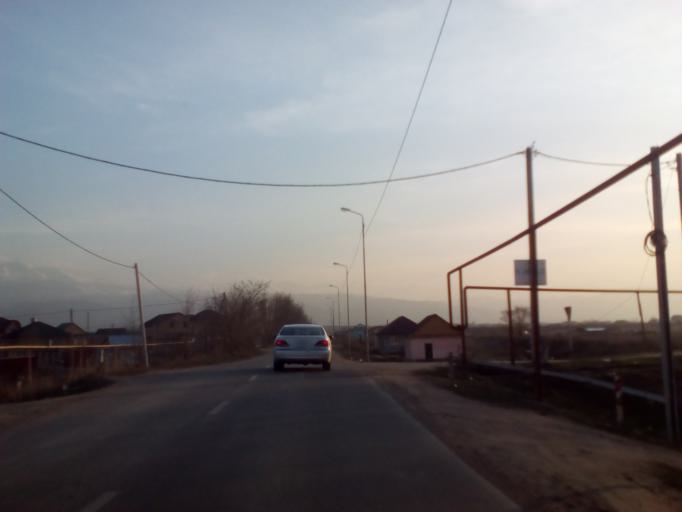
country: KZ
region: Almaty Oblysy
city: Burunday
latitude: 43.2386
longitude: 76.7441
